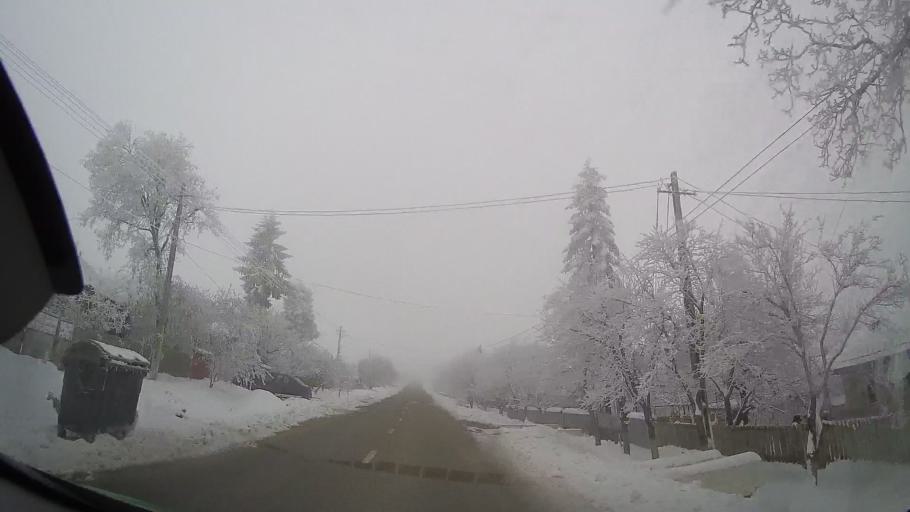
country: RO
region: Neamt
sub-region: Comuna Valea Ursului
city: Valea Ursului
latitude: 46.7993
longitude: 27.0767
